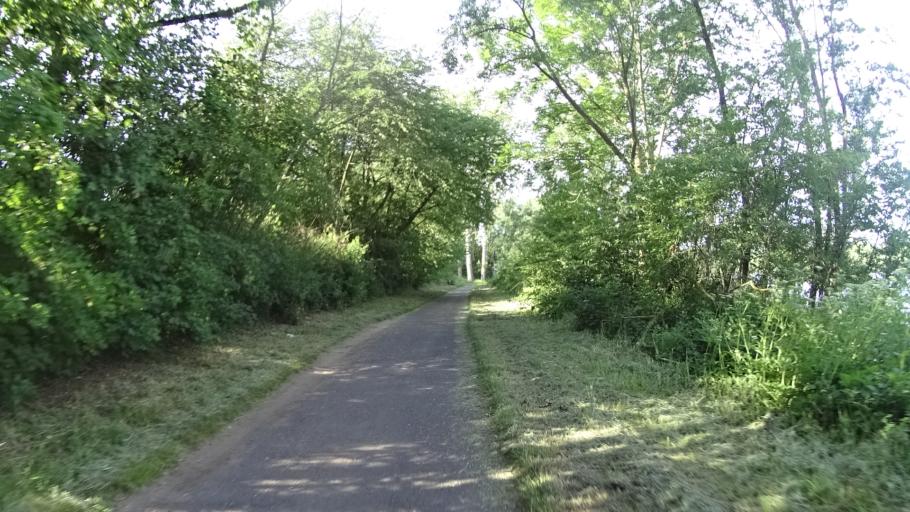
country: DE
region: Bavaria
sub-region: Regierungsbezirk Unterfranken
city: Kahl am Main
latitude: 50.0685
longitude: 8.9922
